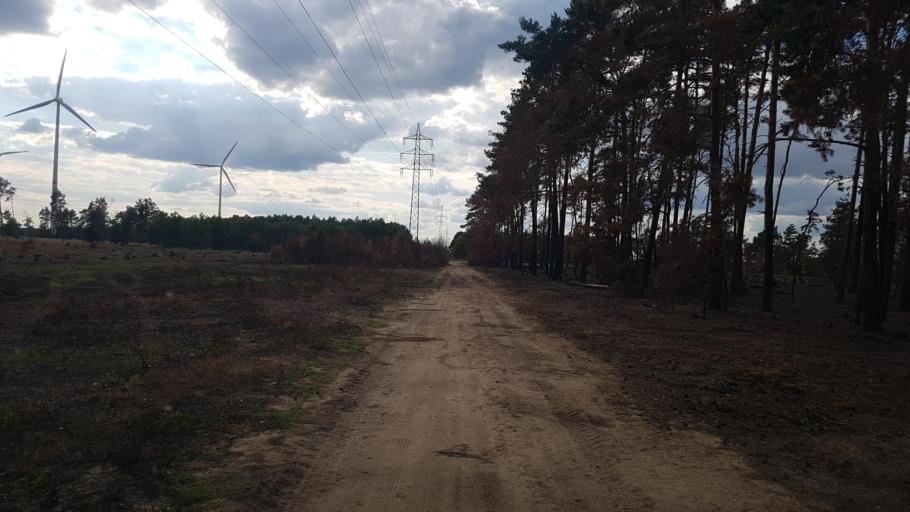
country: DE
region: Saxony
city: Arzberg
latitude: 51.5712
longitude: 13.1813
